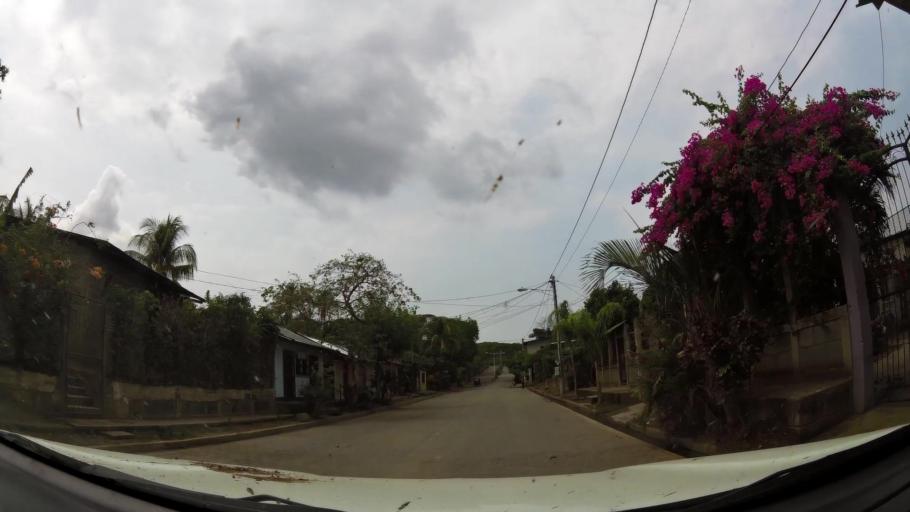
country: NI
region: Granada
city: Diriomo
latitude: 11.8779
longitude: -86.0513
